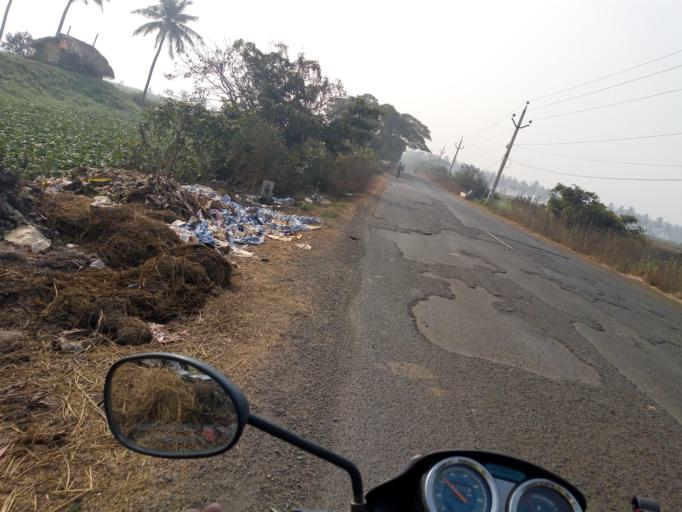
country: IN
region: Andhra Pradesh
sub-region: West Godavari
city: Tadepallegudem
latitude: 16.7708
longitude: 81.4253
